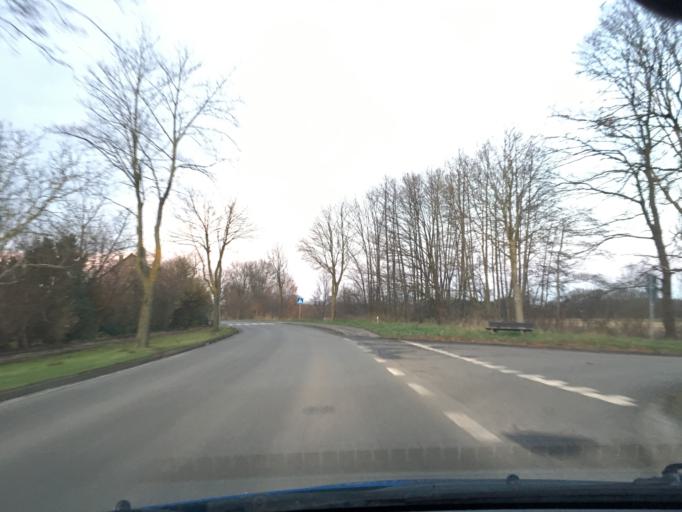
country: DE
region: Lower Saxony
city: Barum
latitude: 53.3643
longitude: 10.4143
